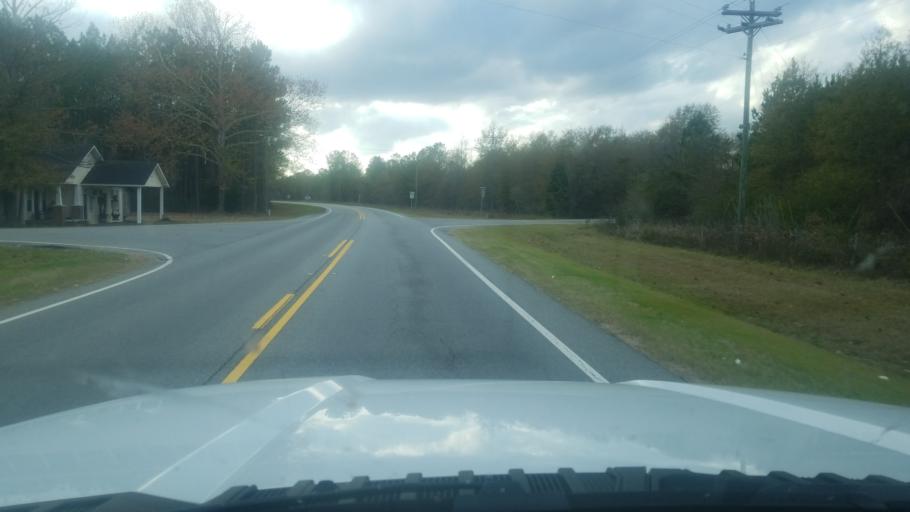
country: US
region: Georgia
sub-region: Evans County
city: Claxton
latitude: 32.1499
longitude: -82.0145
